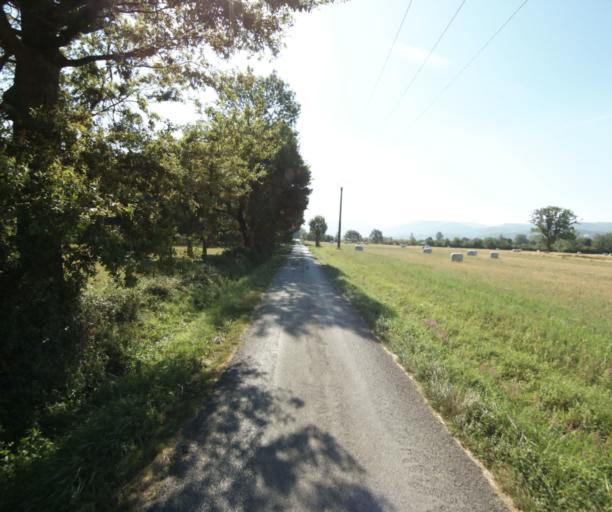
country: FR
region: Midi-Pyrenees
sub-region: Departement de la Haute-Garonne
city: Revel
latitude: 43.4659
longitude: 2.0124
